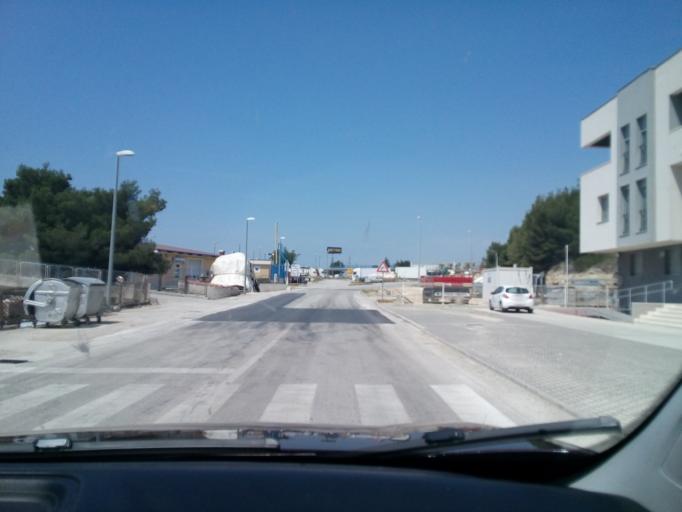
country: HR
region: Splitsko-Dalmatinska
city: Vranjic
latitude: 43.5451
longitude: 16.4592
